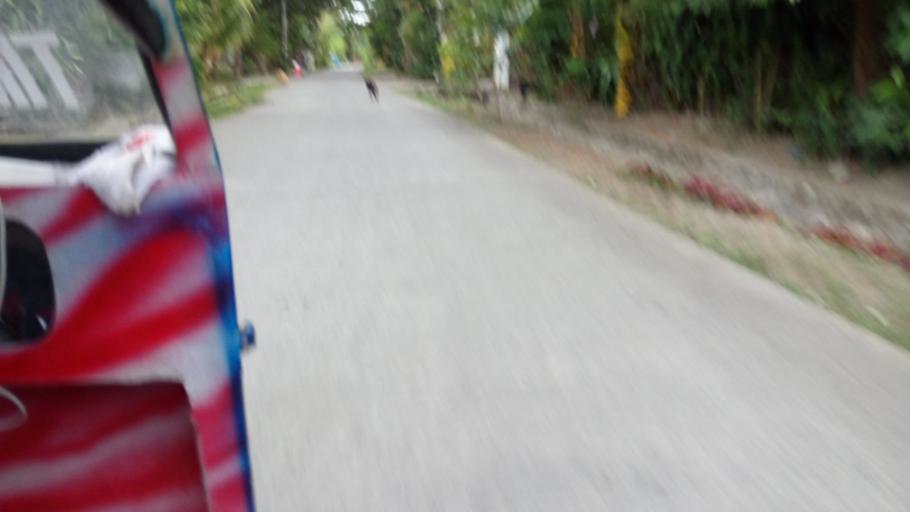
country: PH
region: Ilocos
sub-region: Province of La Union
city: Namboongan
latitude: 16.2924
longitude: 120.3783
